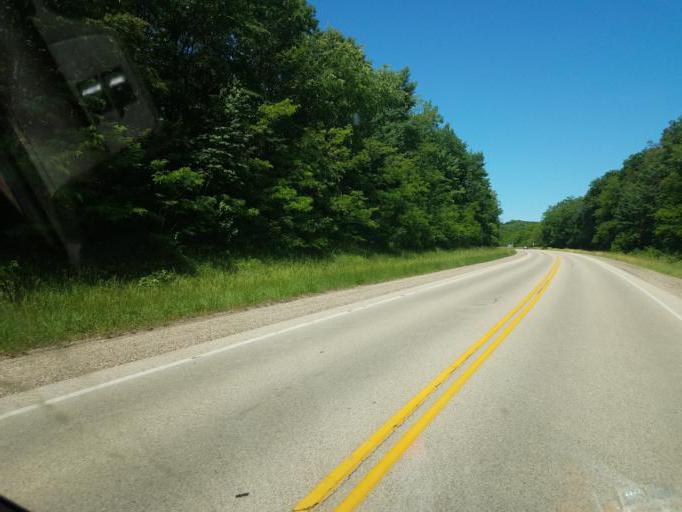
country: US
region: Wisconsin
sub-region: Adams County
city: Adams
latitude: 43.7859
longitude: -89.8625
